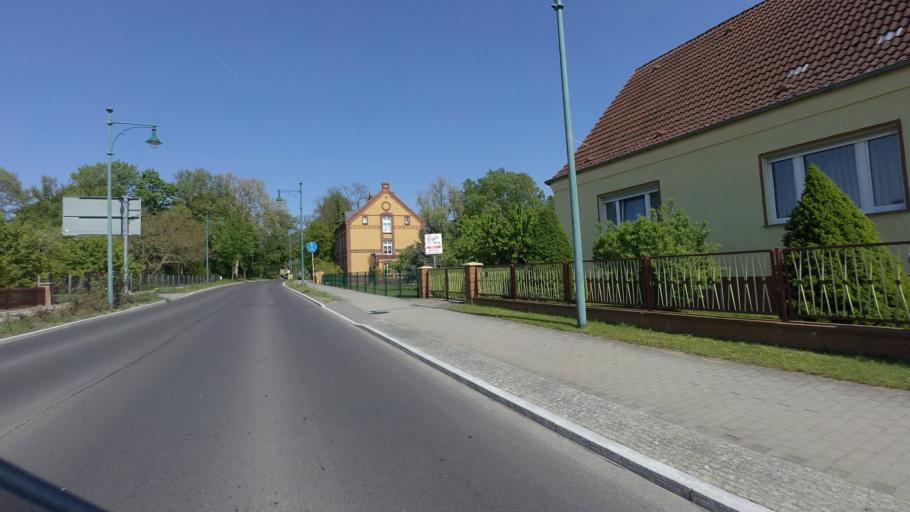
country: DE
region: Brandenburg
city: Beeskow
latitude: 52.1682
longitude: 14.2602
